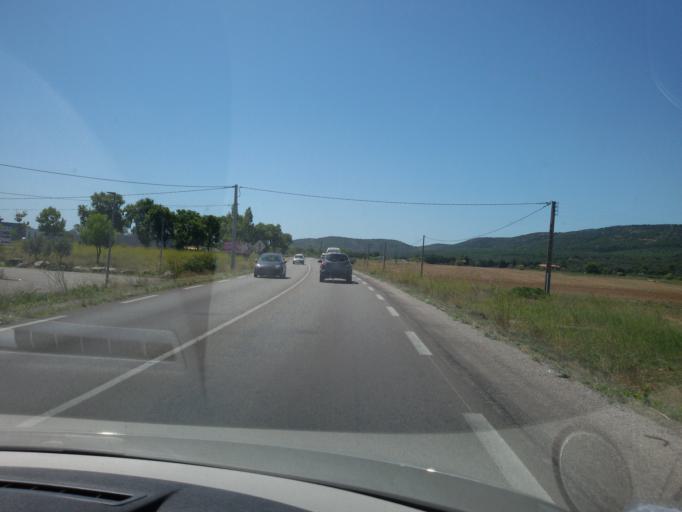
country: FR
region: Languedoc-Roussillon
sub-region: Departement de l'Herault
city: Mireval
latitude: 43.5049
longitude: 3.7917
